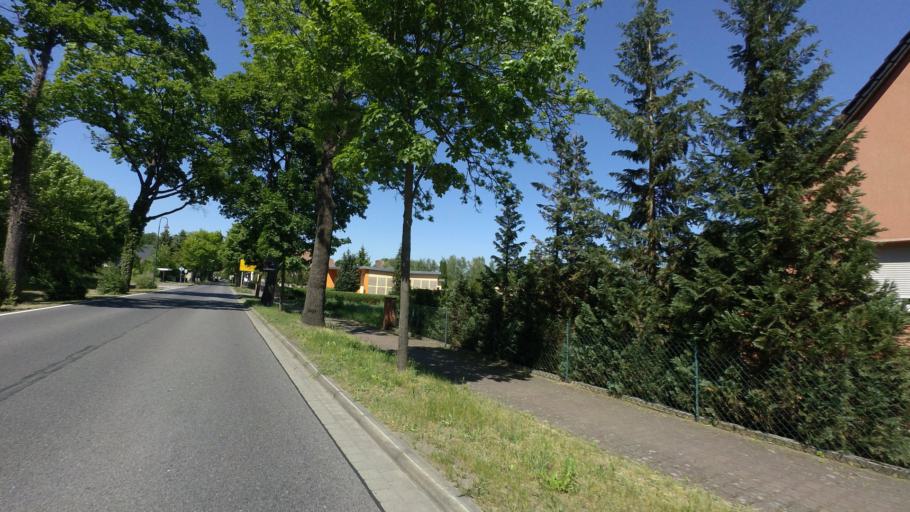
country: DE
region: Brandenburg
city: Lieberose
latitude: 51.9778
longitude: 14.2999
